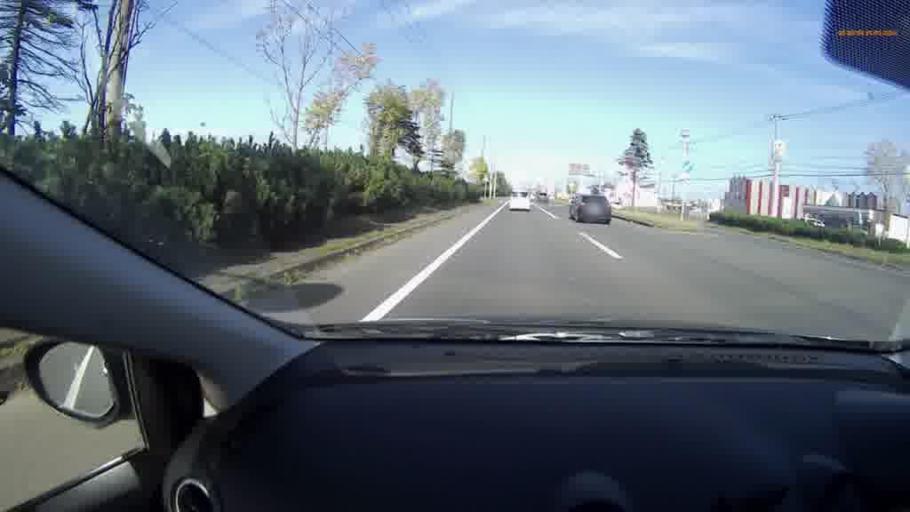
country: JP
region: Hokkaido
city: Kushiro
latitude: 43.0061
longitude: 144.4153
